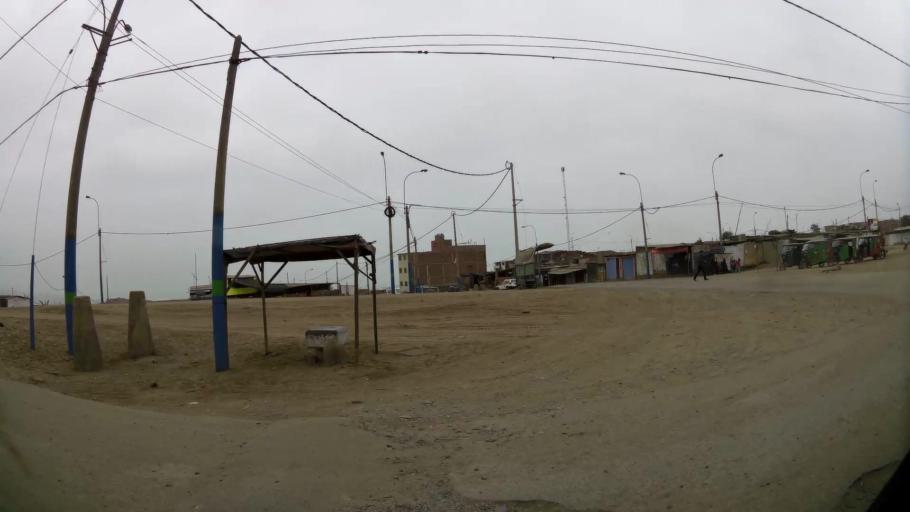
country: PE
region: Lima
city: Ventanilla
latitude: -11.8489
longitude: -77.1374
